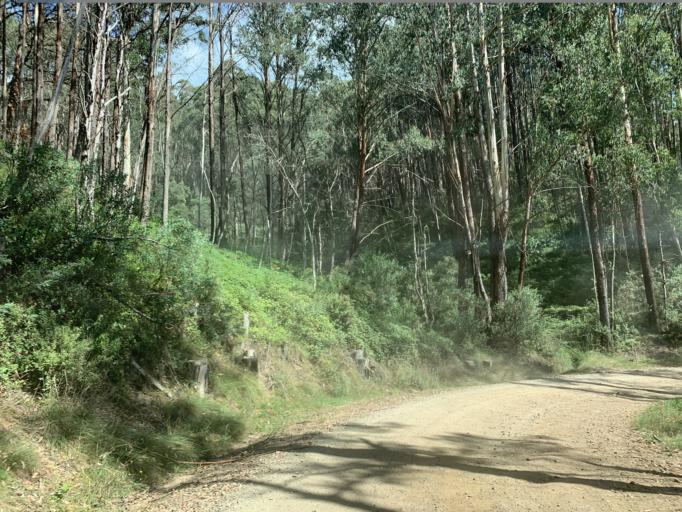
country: AU
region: Victoria
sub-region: Mansfield
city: Mansfield
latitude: -37.0929
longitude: 146.5404
